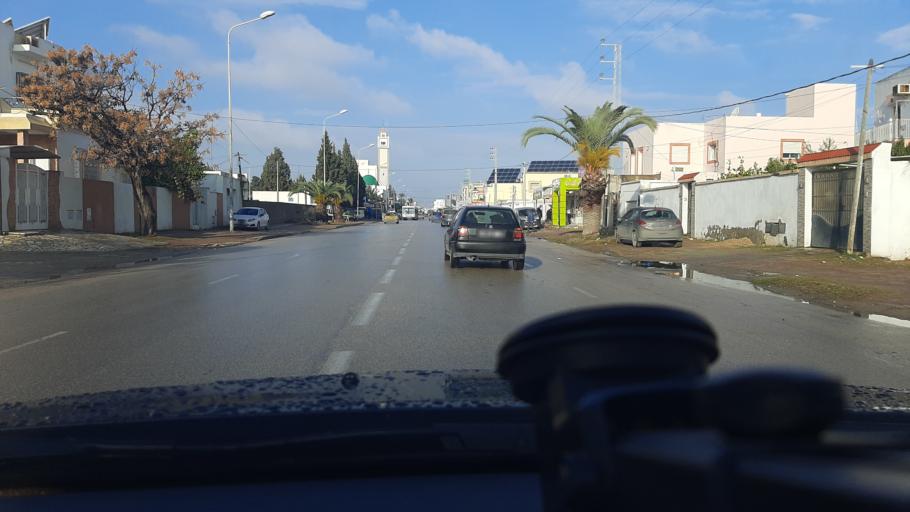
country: TN
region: Safaqis
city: Sfax
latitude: 34.7441
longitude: 10.7305
